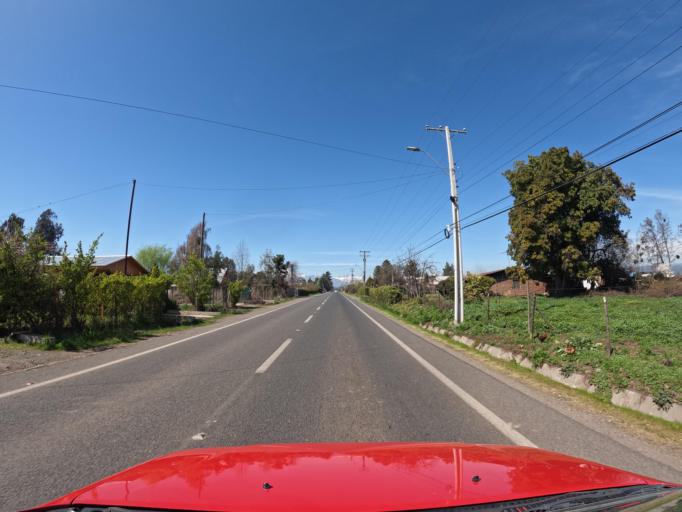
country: CL
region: Maule
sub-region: Provincia de Curico
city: Teno
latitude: -34.9646
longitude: -71.0556
